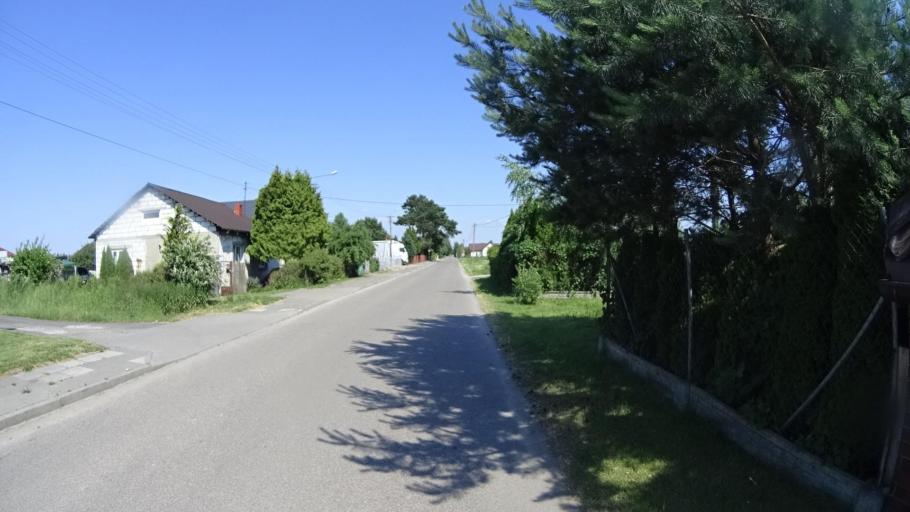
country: PL
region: Masovian Voivodeship
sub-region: Powiat warszawski zachodni
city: Bieniewice
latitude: 52.1911
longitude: 20.5428
